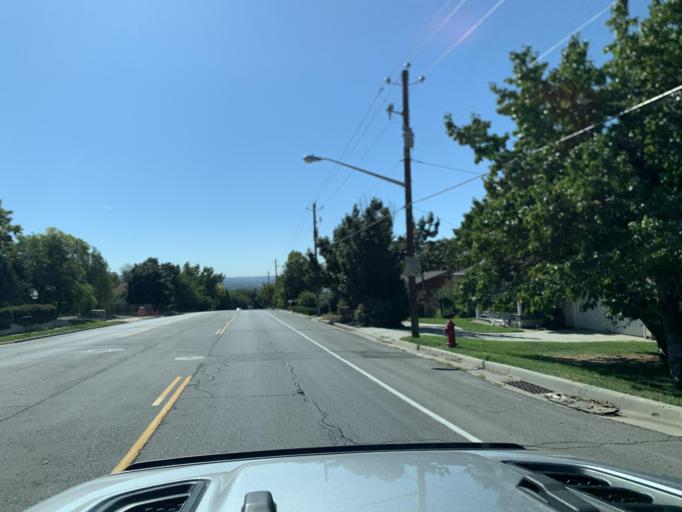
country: US
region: Utah
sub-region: Weber County
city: North Ogden
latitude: 41.3167
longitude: -111.9668
